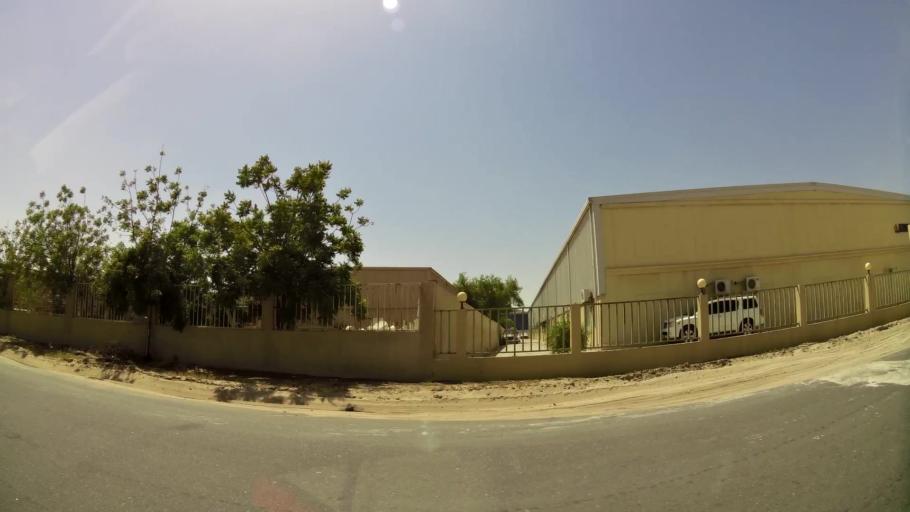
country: AE
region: Dubai
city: Dubai
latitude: 24.9889
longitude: 55.1568
